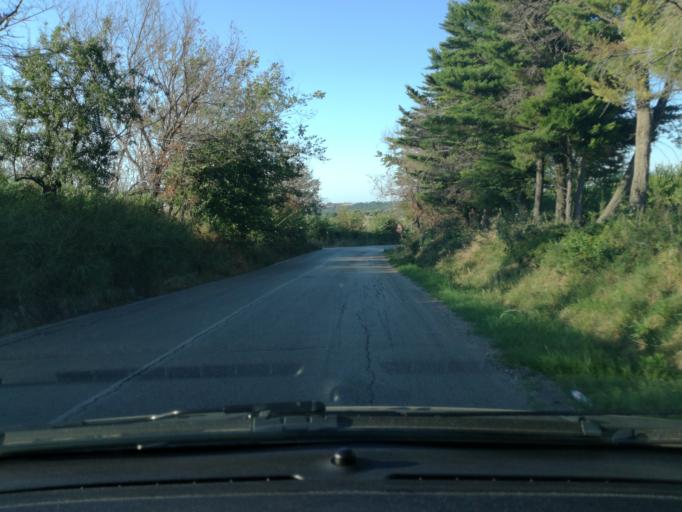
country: IT
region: Molise
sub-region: Provincia di Campobasso
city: Guglionesi
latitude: 41.9309
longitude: 14.9301
